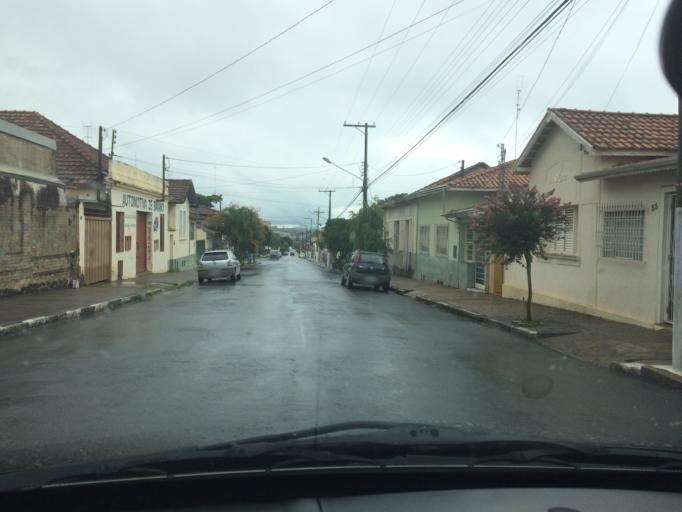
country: BR
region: Sao Paulo
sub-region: Casa Branca
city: Casa Branca
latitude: -21.7746
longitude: -47.0810
